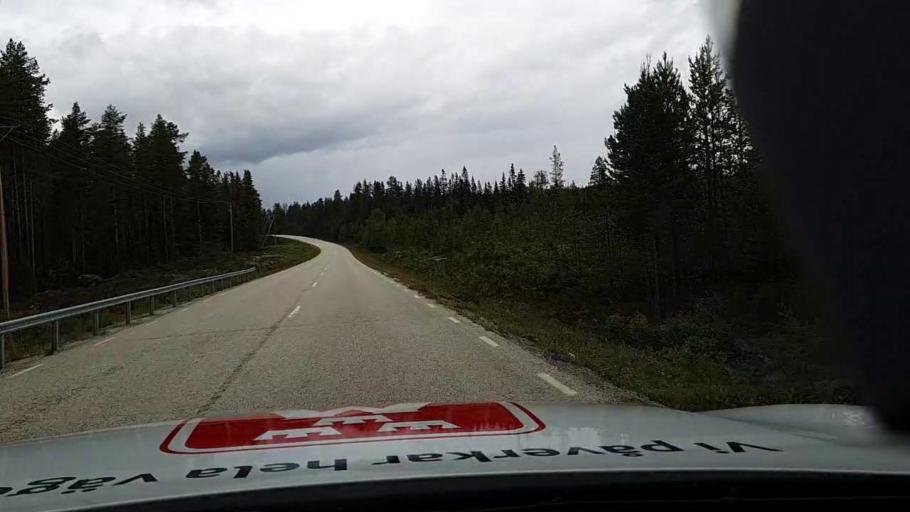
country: SE
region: Jaemtland
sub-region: Are Kommun
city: Jarpen
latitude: 62.7966
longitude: 13.6779
